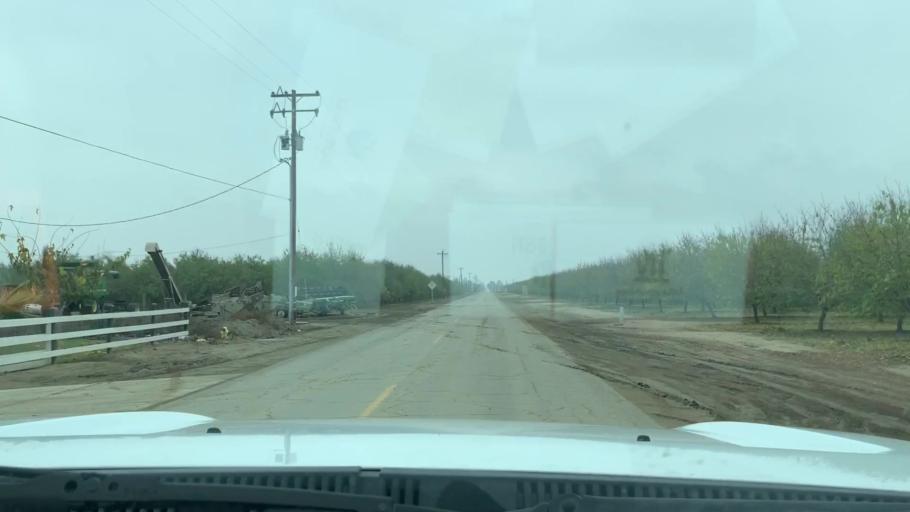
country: US
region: California
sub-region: Kern County
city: Shafter
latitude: 35.4781
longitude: -119.2944
